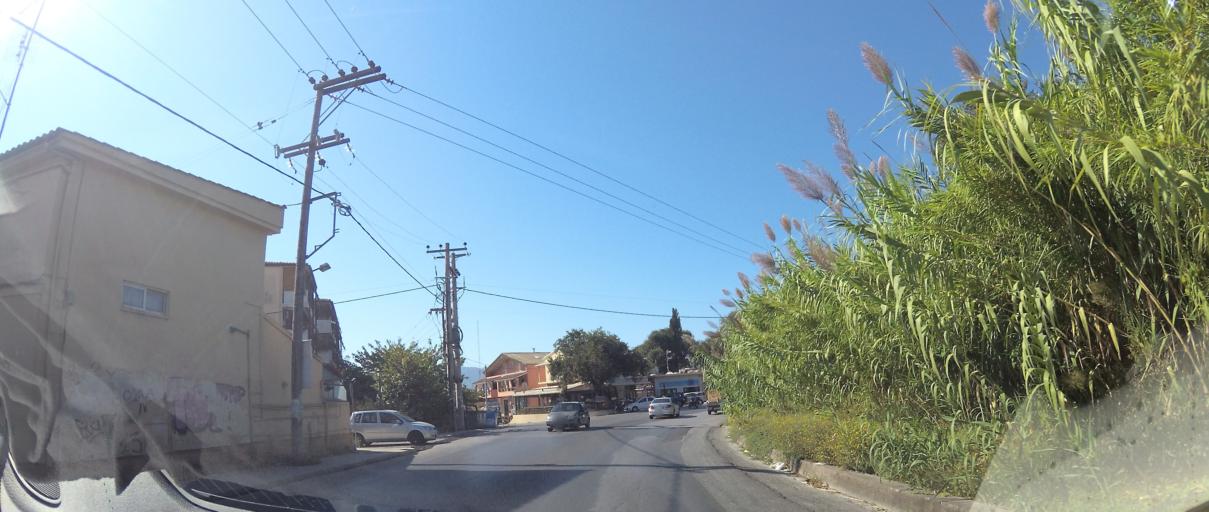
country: GR
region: Ionian Islands
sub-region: Nomos Kerkyras
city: Alepou
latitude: 39.6151
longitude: 19.9036
